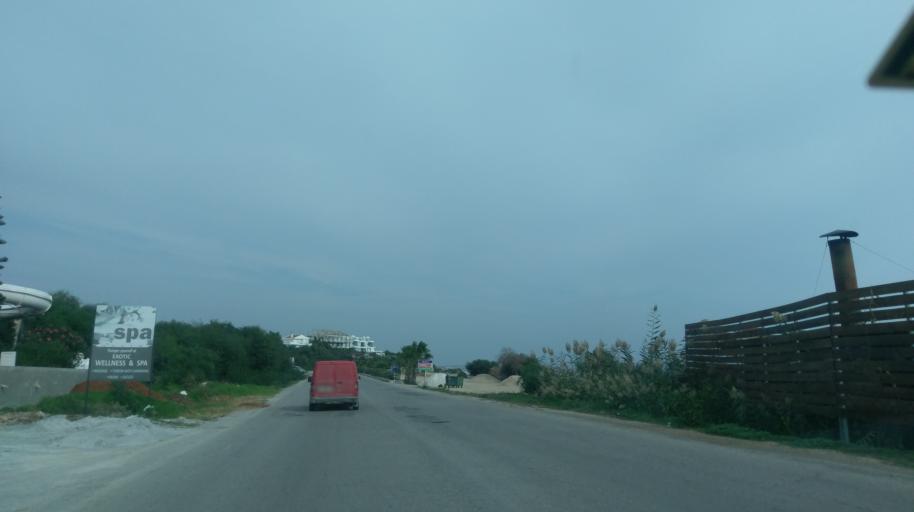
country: CY
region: Ammochostos
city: Trikomo
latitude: 35.3069
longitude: 33.9449
